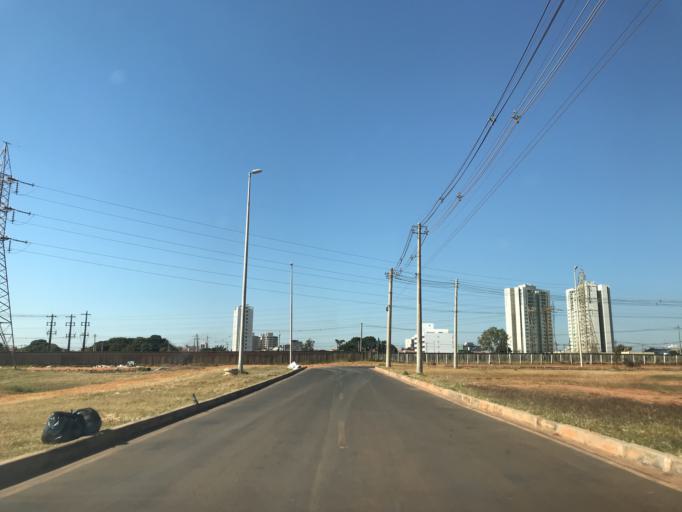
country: BR
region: Federal District
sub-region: Brasilia
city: Brasilia
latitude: -15.8489
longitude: -48.0386
